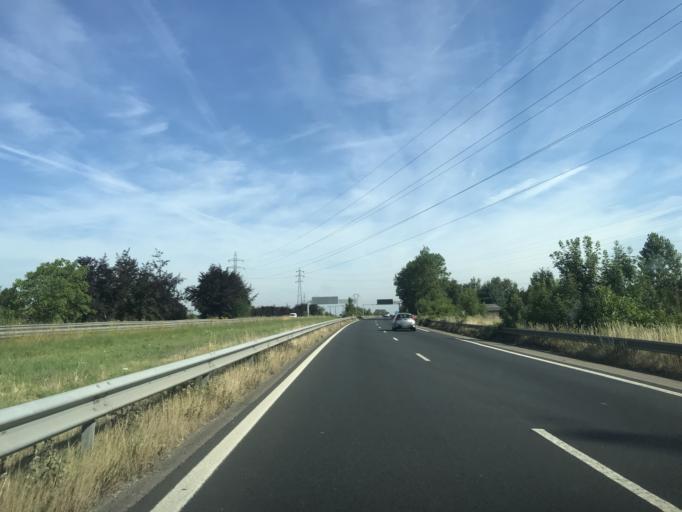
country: FR
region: Haute-Normandie
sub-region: Departement de la Seine-Maritime
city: La Vaupaliere
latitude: 49.4876
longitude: 1.0013
